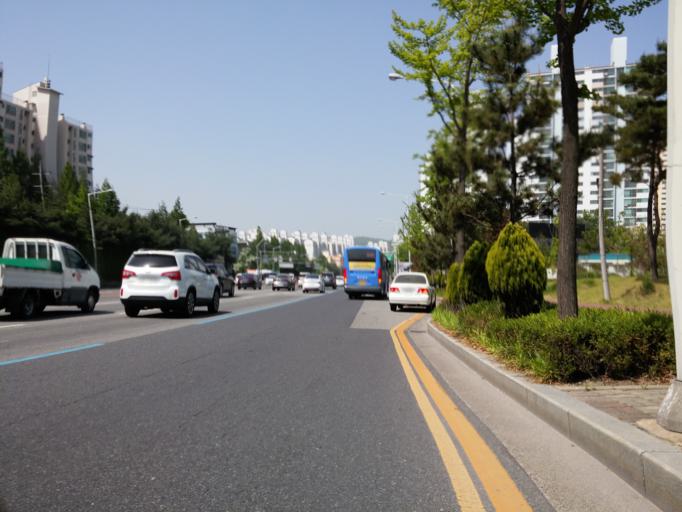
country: KR
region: Daejeon
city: Daejeon
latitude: 36.3030
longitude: 127.3425
